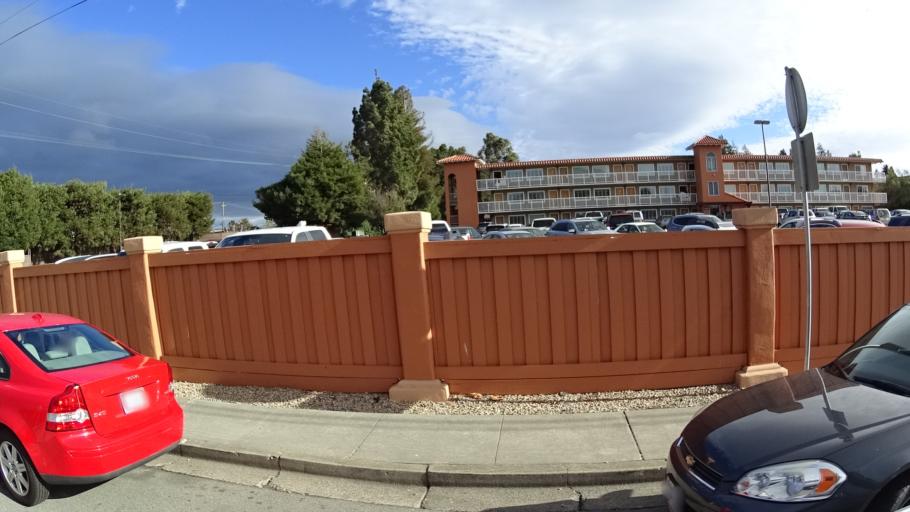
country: US
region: California
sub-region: San Mateo County
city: Millbrae
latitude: 37.6090
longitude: -122.3971
